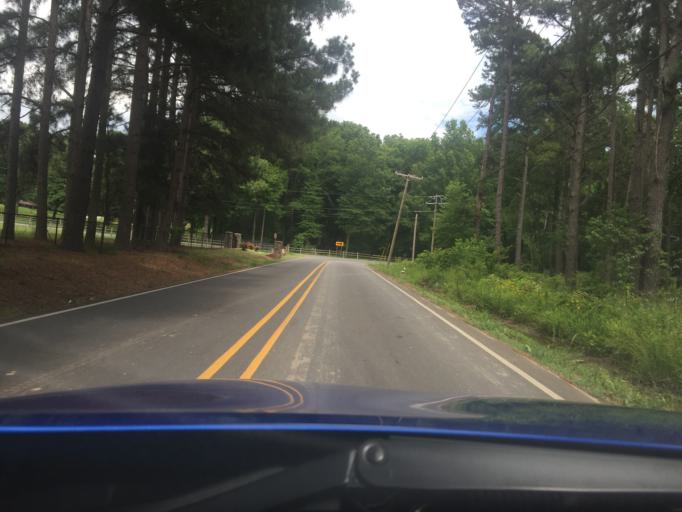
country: US
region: Arkansas
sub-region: Pulaski County
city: Maumelle
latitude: 34.8298
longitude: -92.4369
